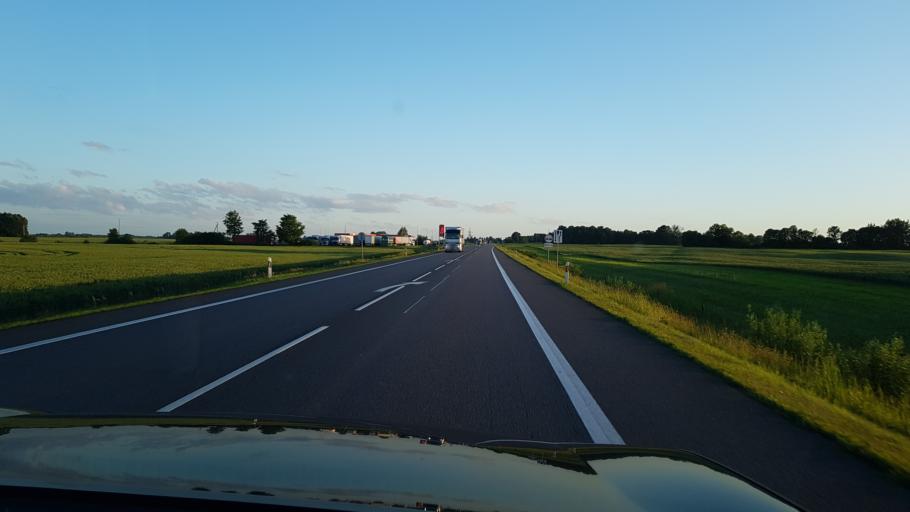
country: LT
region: Kauno apskritis
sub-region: Kauno rajonas
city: Mastaiciai
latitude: 54.7407
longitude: 23.7140
